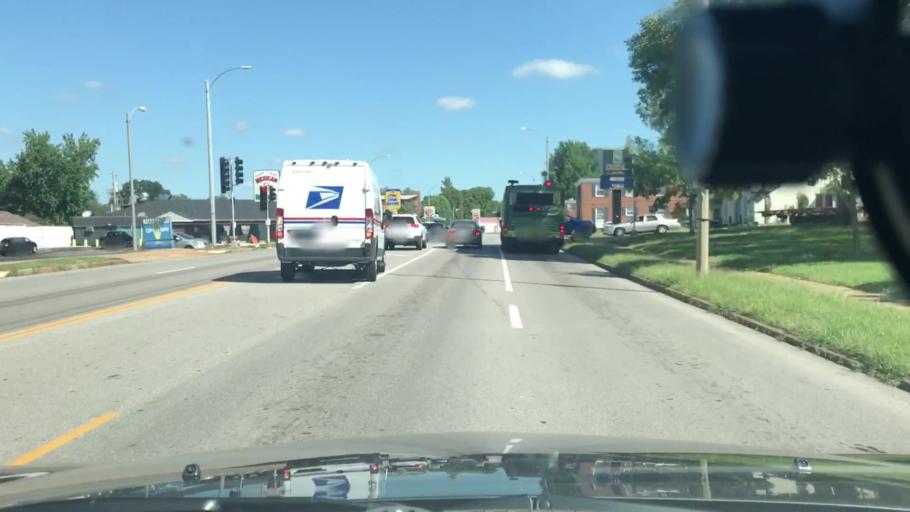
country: US
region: Missouri
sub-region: Saint Louis County
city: Maplewood
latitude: 38.6015
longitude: -90.2920
